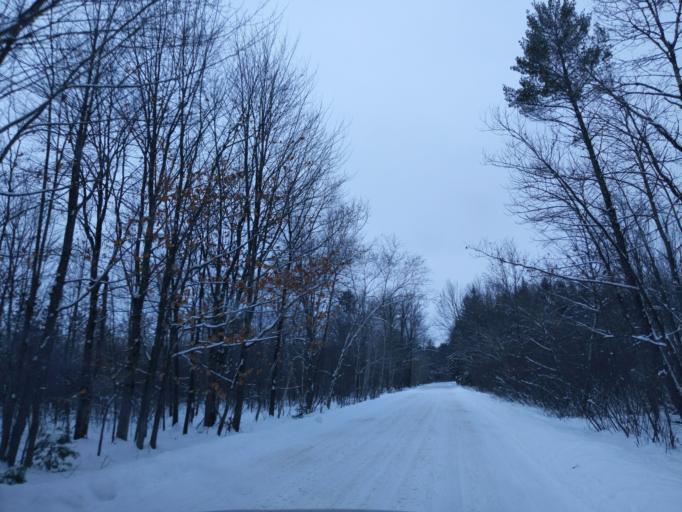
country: US
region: Wisconsin
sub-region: Marathon County
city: Mosinee
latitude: 44.7600
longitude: -89.8646
